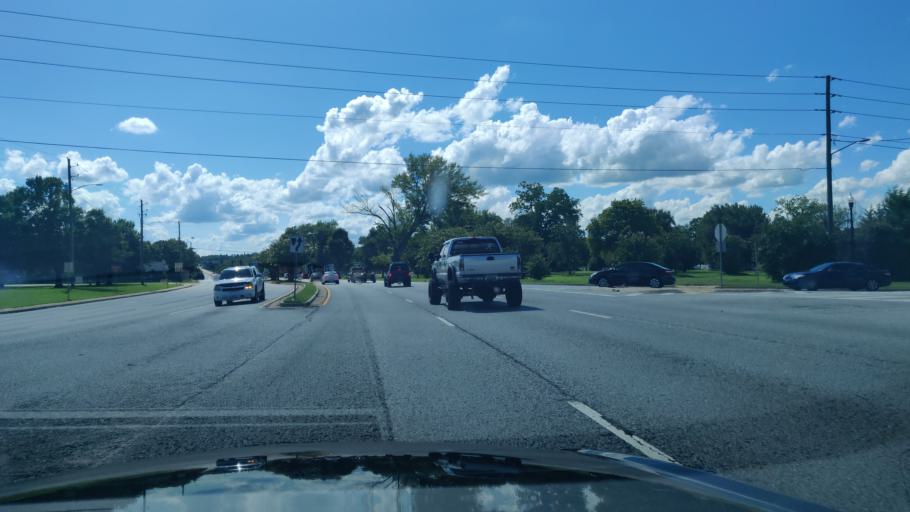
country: US
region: Georgia
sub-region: Muscogee County
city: Columbus
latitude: 32.4532
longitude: -84.9848
